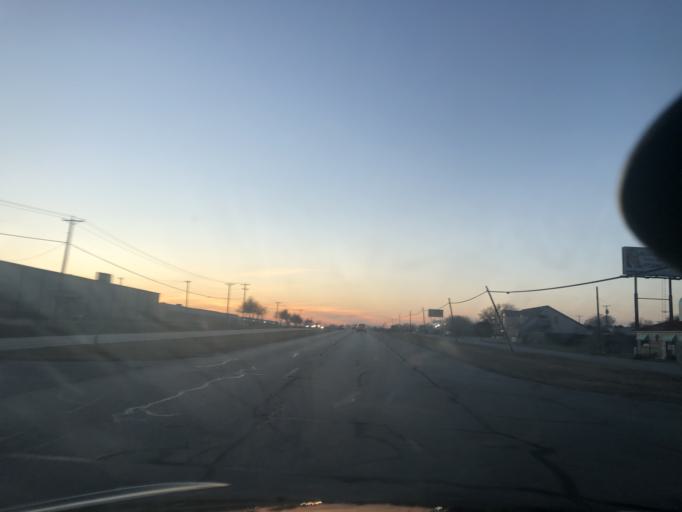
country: US
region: Texas
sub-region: Tarrant County
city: White Settlement
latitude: 32.7247
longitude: -97.4872
